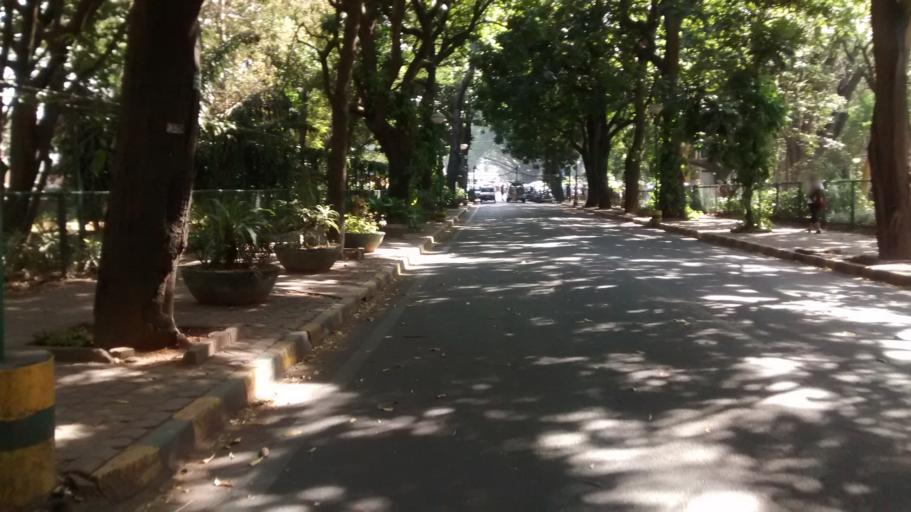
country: IN
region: Karnataka
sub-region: Bangalore Urban
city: Bangalore
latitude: 12.9733
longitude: 77.5937
